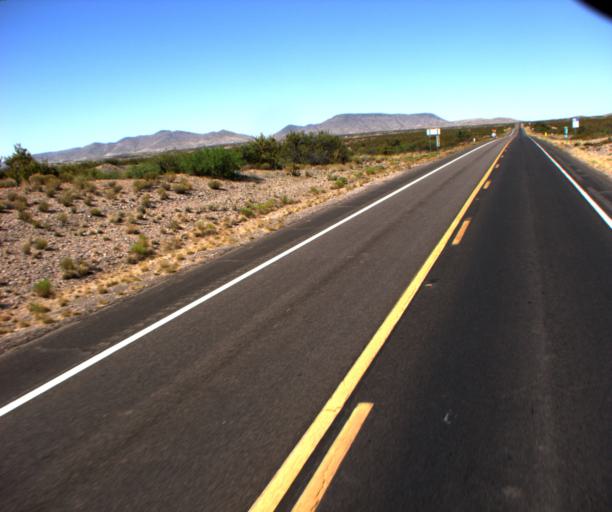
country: US
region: Arizona
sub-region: Greenlee County
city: Clifton
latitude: 32.7383
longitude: -109.1425
